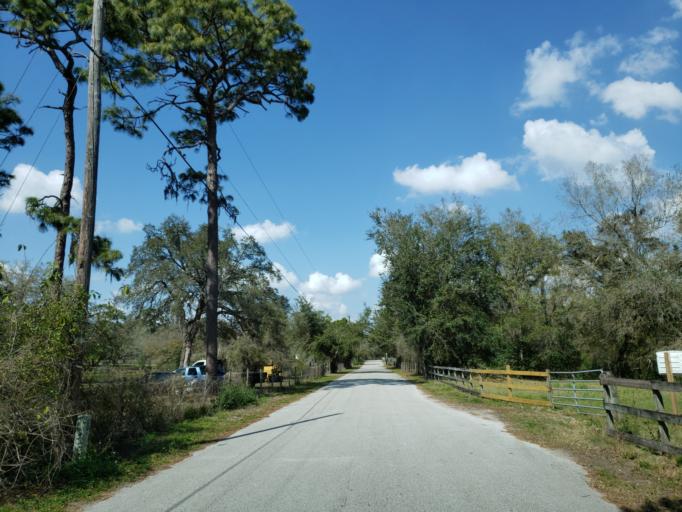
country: US
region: Florida
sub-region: Hillsborough County
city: Keystone
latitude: 28.1522
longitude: -82.6409
